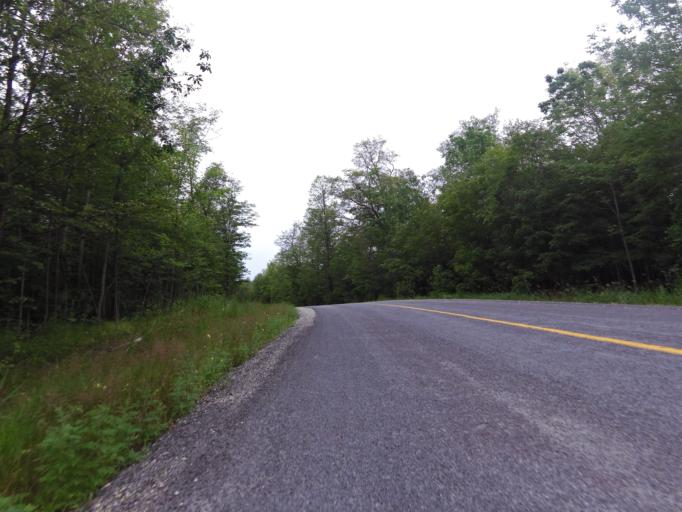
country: CA
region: Ontario
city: Perth
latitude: 44.8788
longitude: -76.5293
